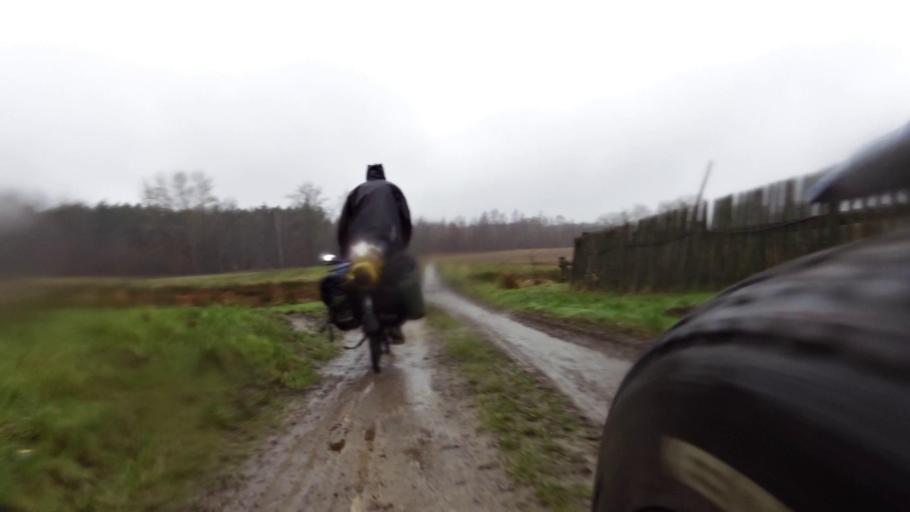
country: PL
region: West Pomeranian Voivodeship
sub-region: Powiat drawski
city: Wierzchowo
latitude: 53.5228
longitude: 16.1449
